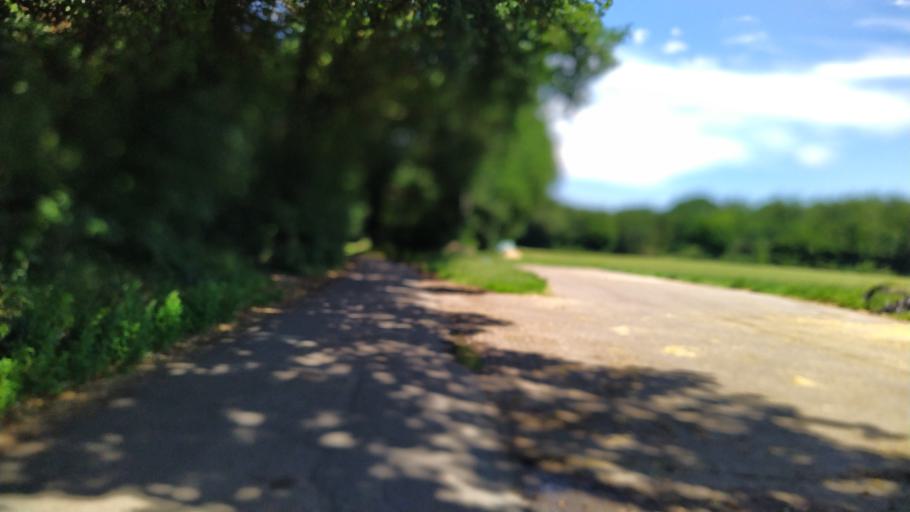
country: DE
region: Lower Saxony
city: Bargstedt
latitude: 53.4959
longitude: 9.4364
